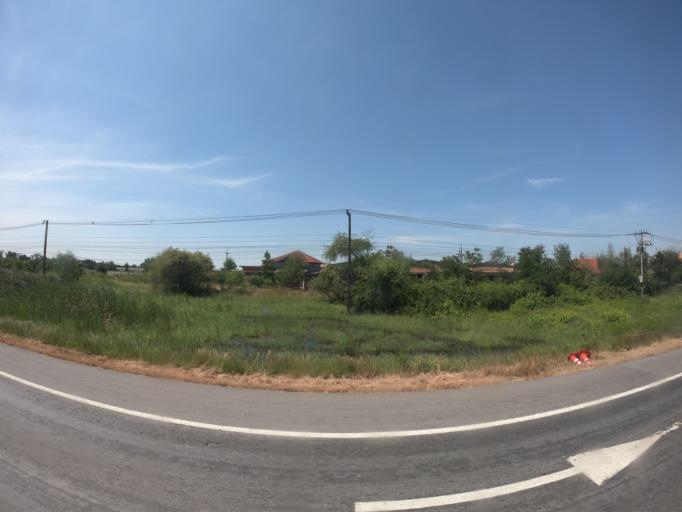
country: TH
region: Khon Kaen
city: Phon
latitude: 15.7932
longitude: 102.6070
